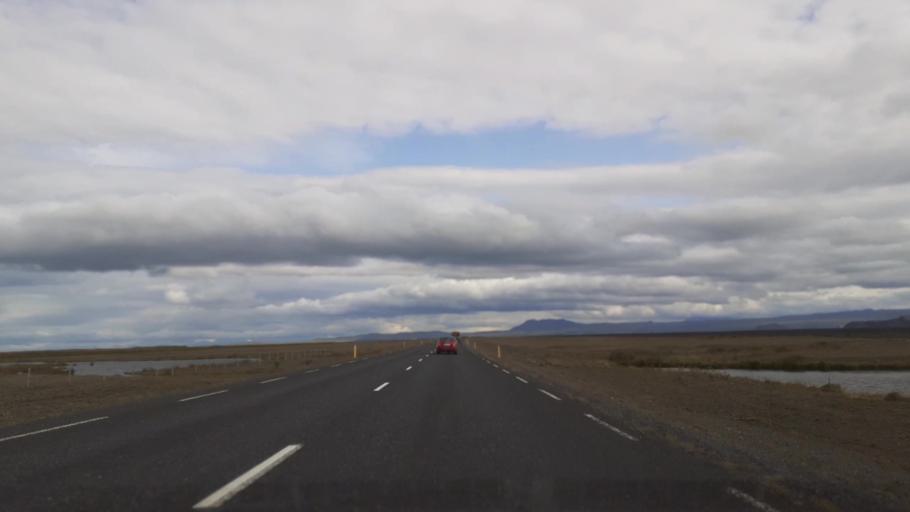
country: IS
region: South
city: Vestmannaeyjar
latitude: 63.5681
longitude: -20.0622
